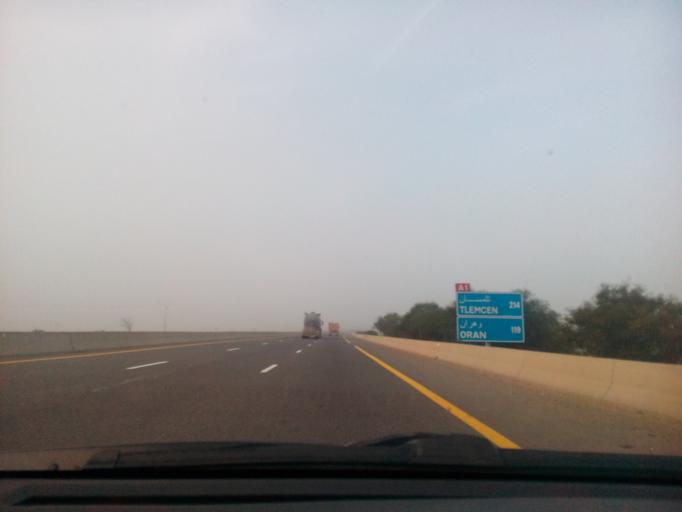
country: DZ
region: Relizane
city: Relizane
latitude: 35.7912
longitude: 0.4757
